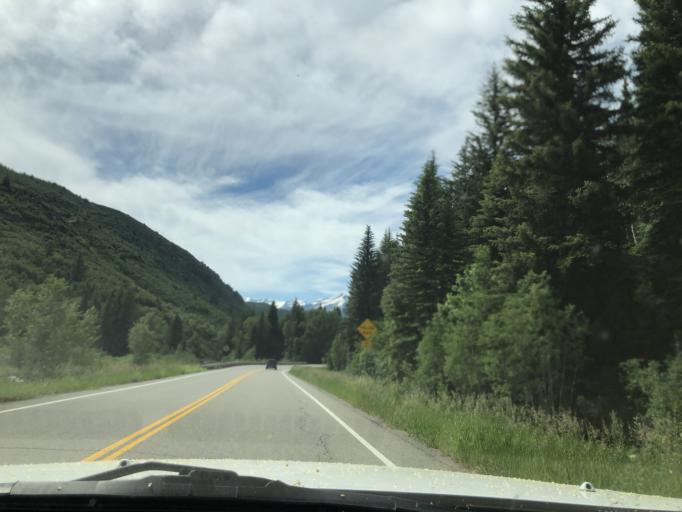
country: US
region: Colorado
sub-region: Delta County
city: Paonia
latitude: 38.9894
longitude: -107.3494
